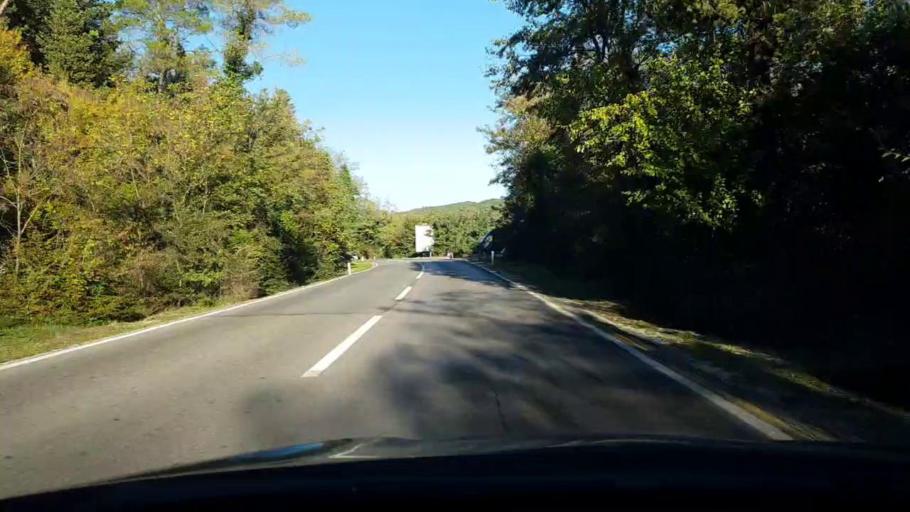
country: ME
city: Igalo
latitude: 42.4782
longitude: 18.4616
